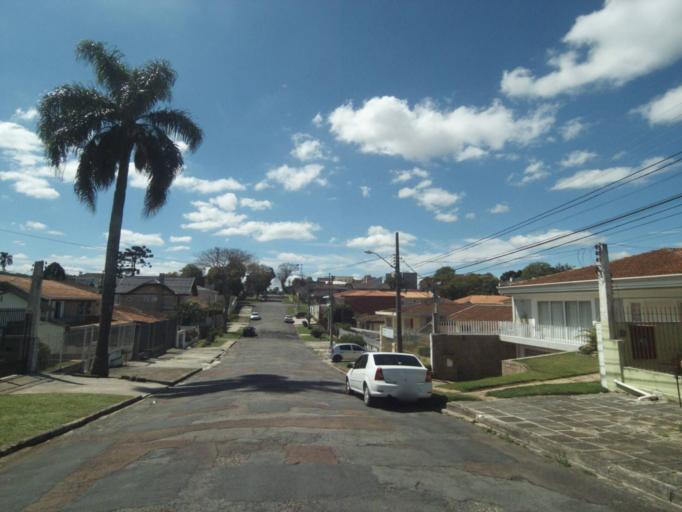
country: BR
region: Parana
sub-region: Curitiba
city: Curitiba
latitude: -25.4019
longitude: -49.2732
